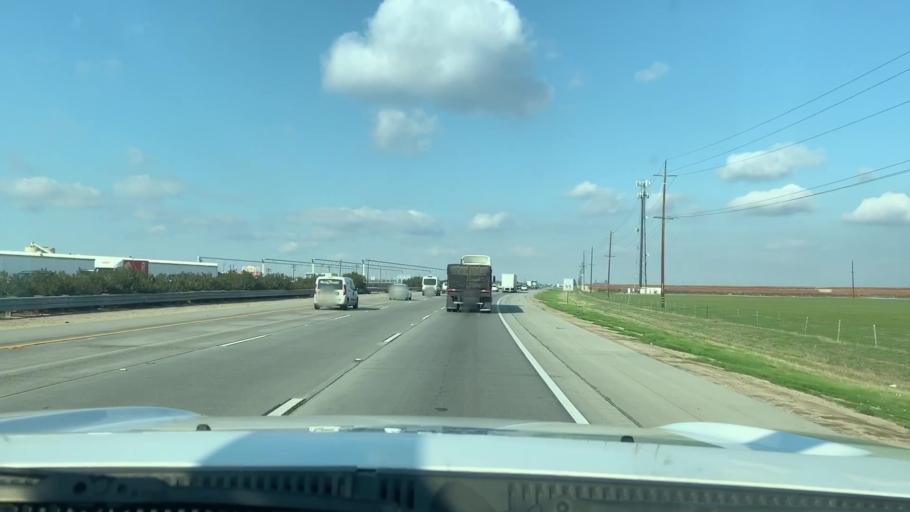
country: US
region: California
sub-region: Kern County
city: Shafter
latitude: 35.5627
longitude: -119.1988
